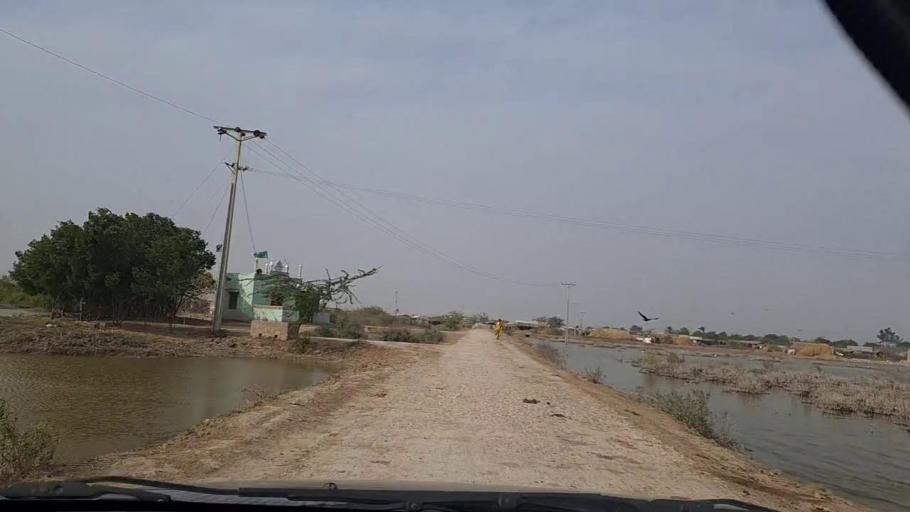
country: PK
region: Sindh
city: Thatta
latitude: 24.5855
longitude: 67.9081
